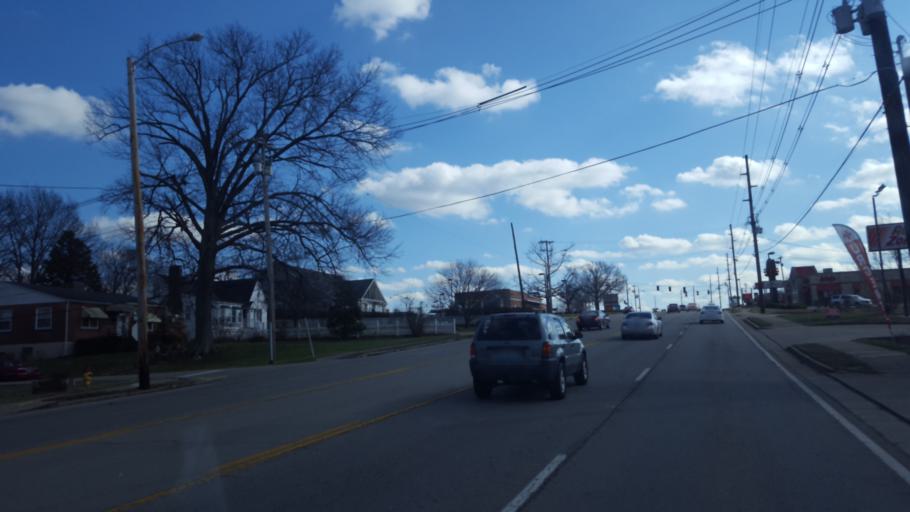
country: US
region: Kentucky
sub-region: Franklin County
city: Frankfort
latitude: 38.1993
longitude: -84.8313
